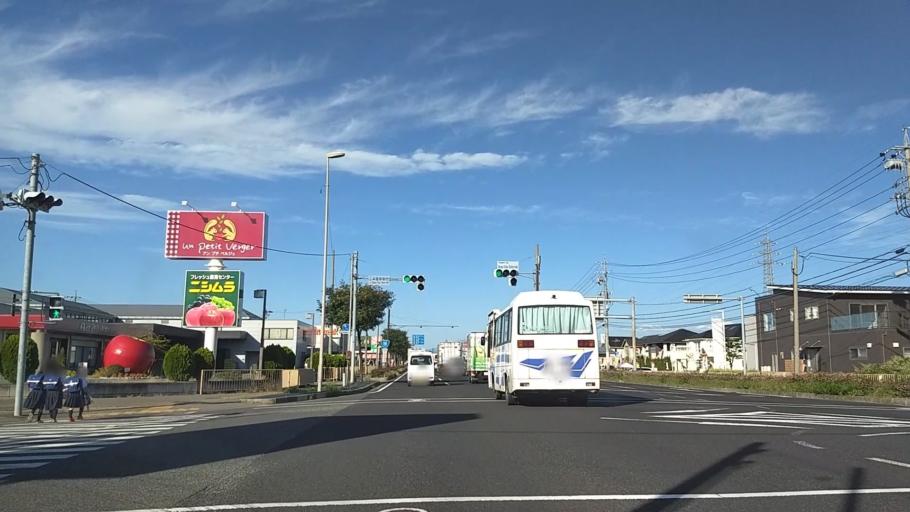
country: JP
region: Nagano
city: Nagano-shi
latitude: 36.5749
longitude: 138.1557
